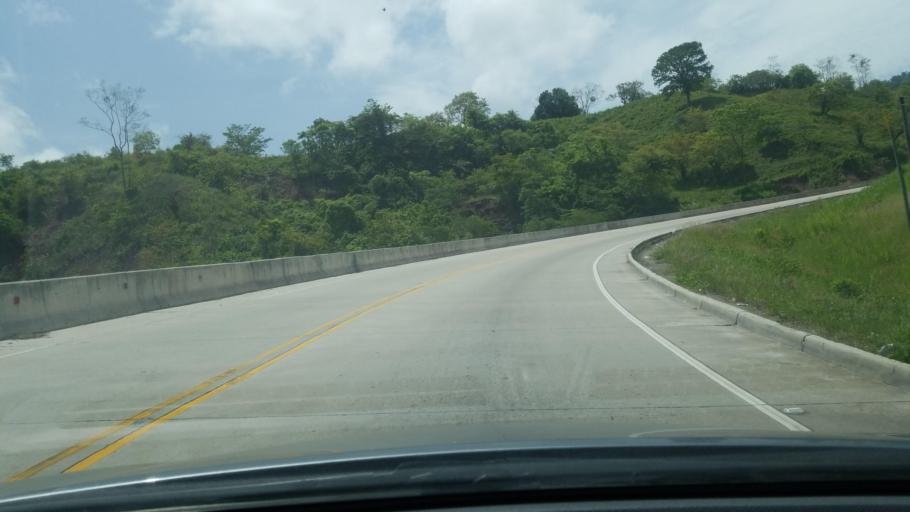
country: HN
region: Copan
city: Agua Caliente
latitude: 14.8760
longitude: -88.7780
